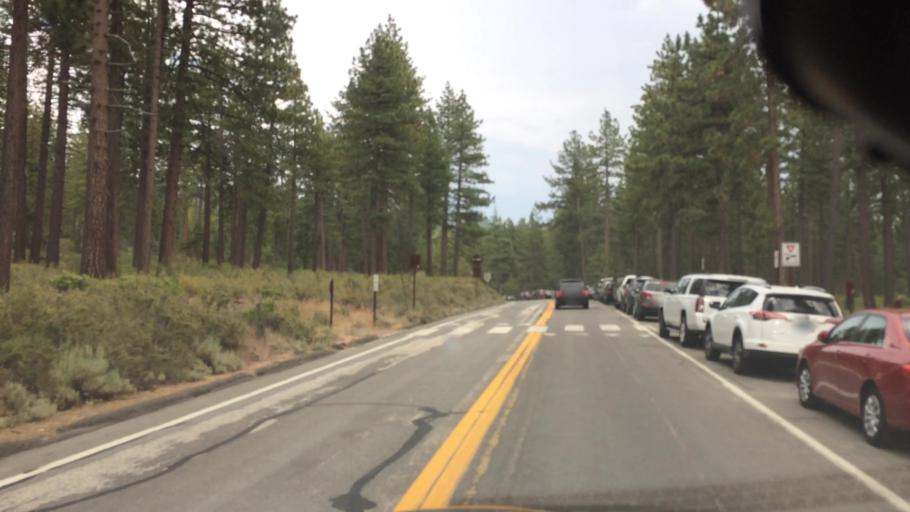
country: US
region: Nevada
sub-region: Douglas County
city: Kingsbury
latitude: 38.9818
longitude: -119.9495
